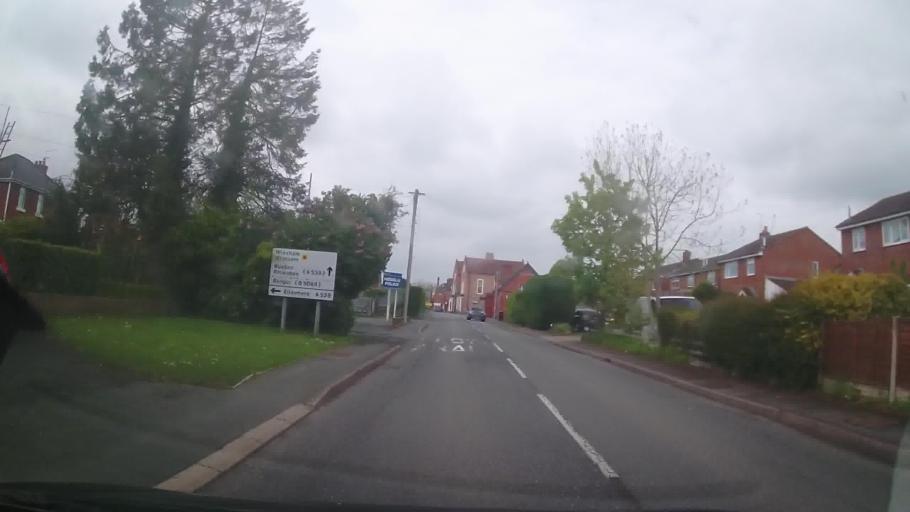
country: GB
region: Wales
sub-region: Wrexham
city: Overton
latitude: 52.9679
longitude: -2.9327
